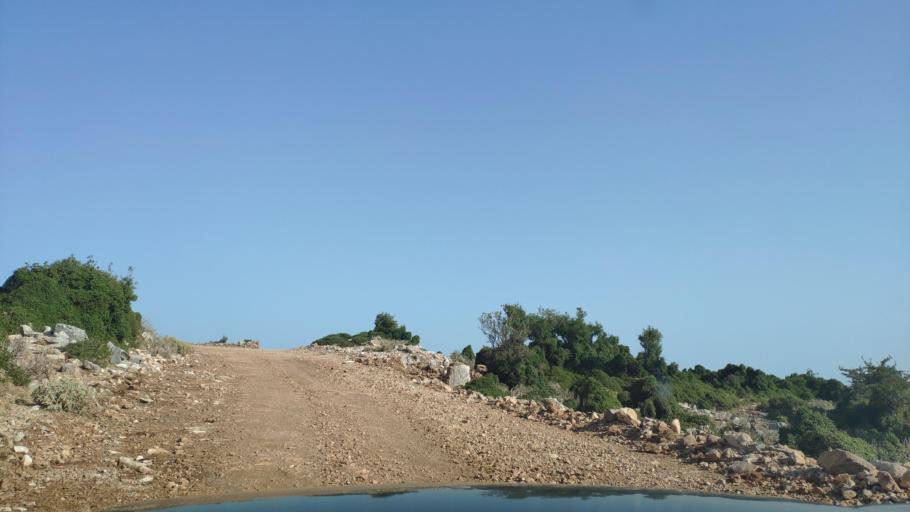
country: GR
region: West Greece
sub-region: Nomos Aitolias kai Akarnanias
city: Monastirakion
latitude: 38.8350
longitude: 20.9759
